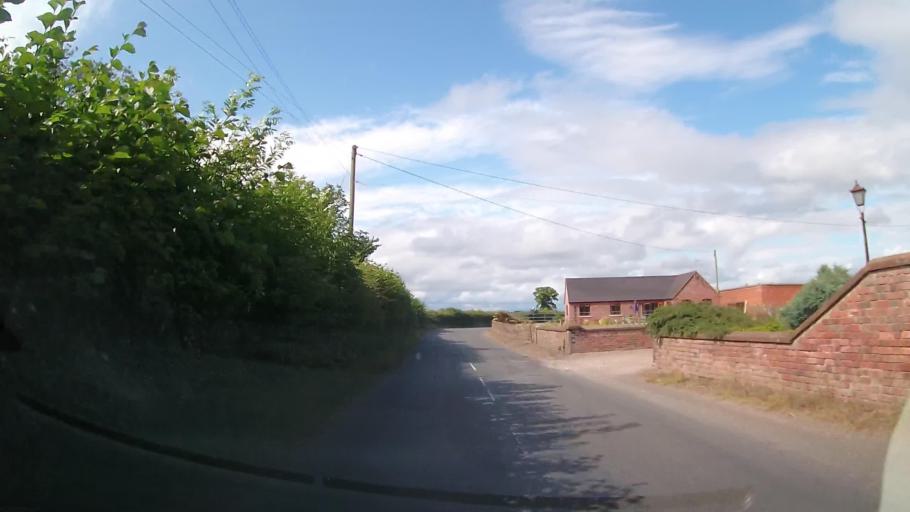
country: GB
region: England
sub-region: Shropshire
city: Petton
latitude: 52.8304
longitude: -2.8053
